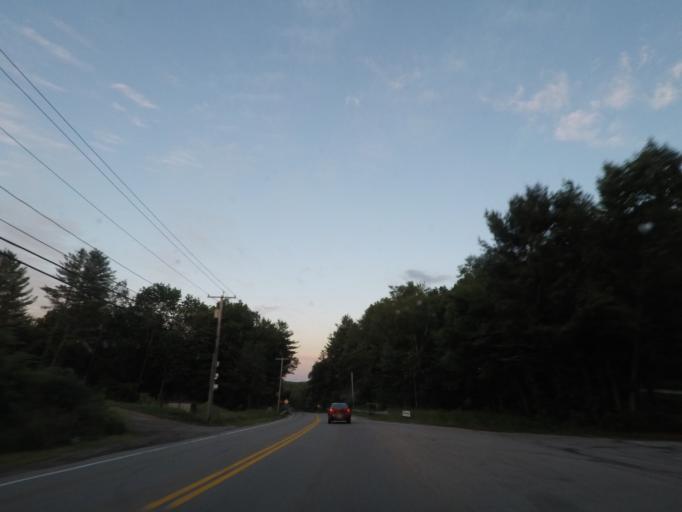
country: US
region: Massachusetts
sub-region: Worcester County
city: Southbridge
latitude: 42.0605
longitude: -72.0027
